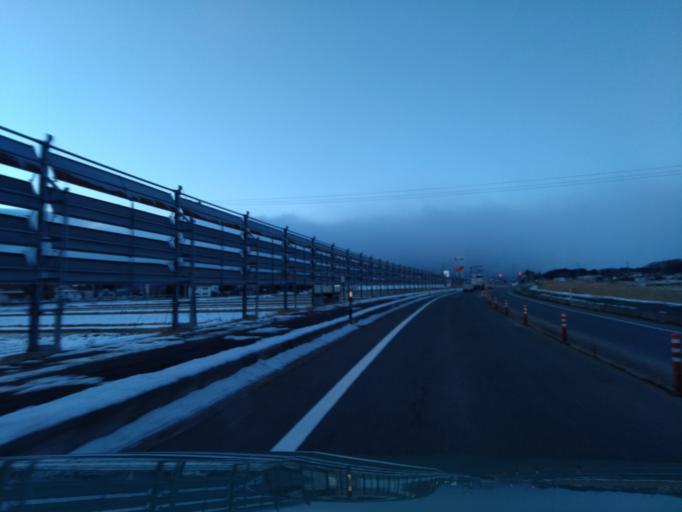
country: JP
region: Iwate
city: Shizukuishi
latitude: 39.6937
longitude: 140.9808
